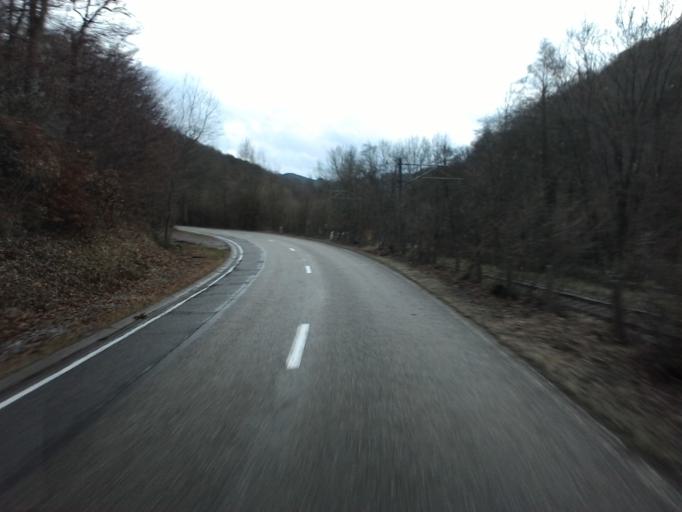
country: BE
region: Wallonia
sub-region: Province de Liege
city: Aywaille
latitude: 50.4381
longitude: 5.7347
